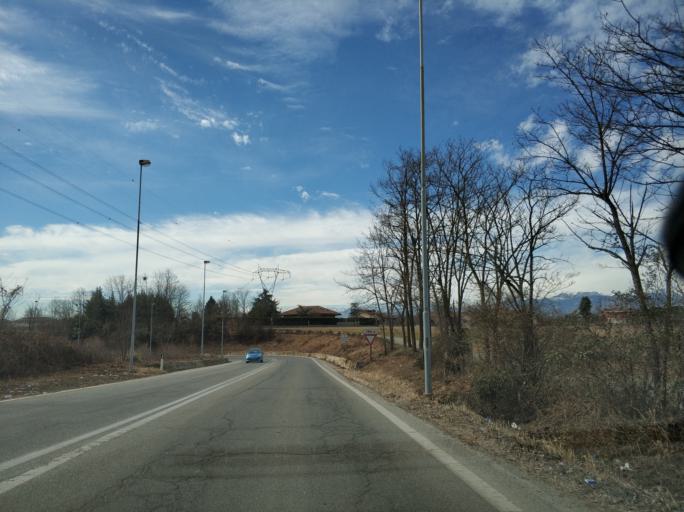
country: IT
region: Piedmont
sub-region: Provincia di Torino
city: Lombardore
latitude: 45.2142
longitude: 7.7297
